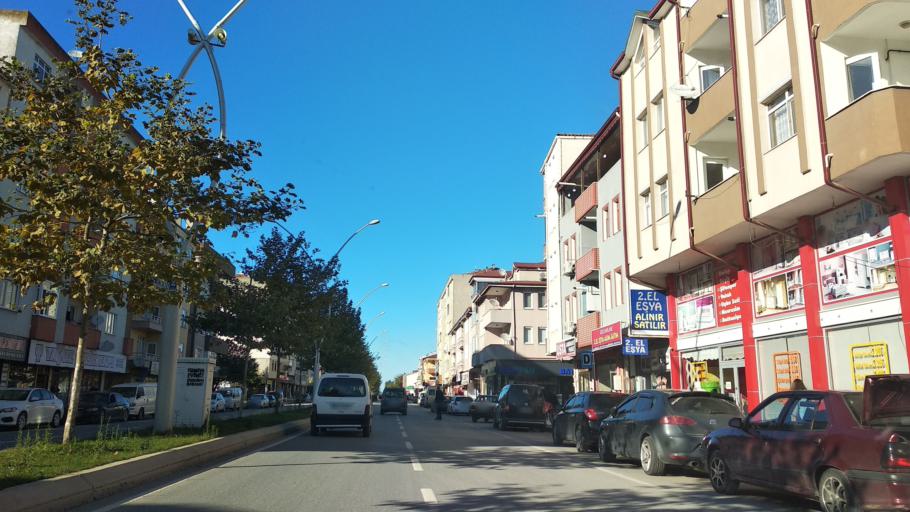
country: TR
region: Sakarya
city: Karasu
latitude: 41.1008
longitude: 30.6926
